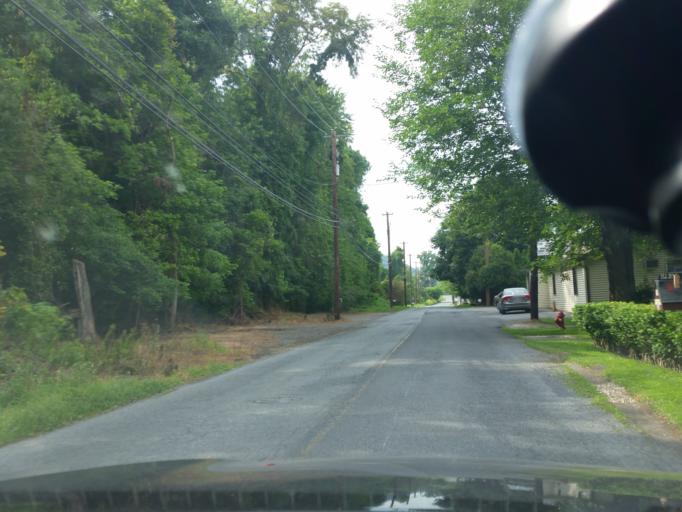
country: US
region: Pennsylvania
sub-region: Perry County
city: Marysville
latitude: 40.3361
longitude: -76.9230
